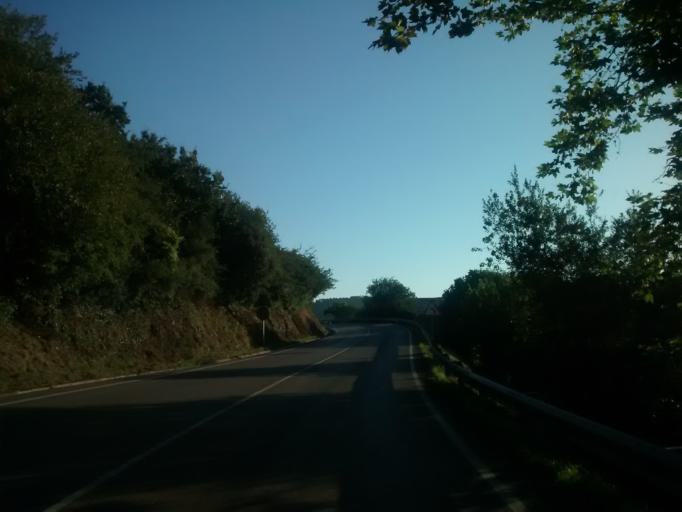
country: ES
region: Cantabria
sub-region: Provincia de Cantabria
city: San Miguel de Meruelo
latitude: 43.4626
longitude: -3.5851
